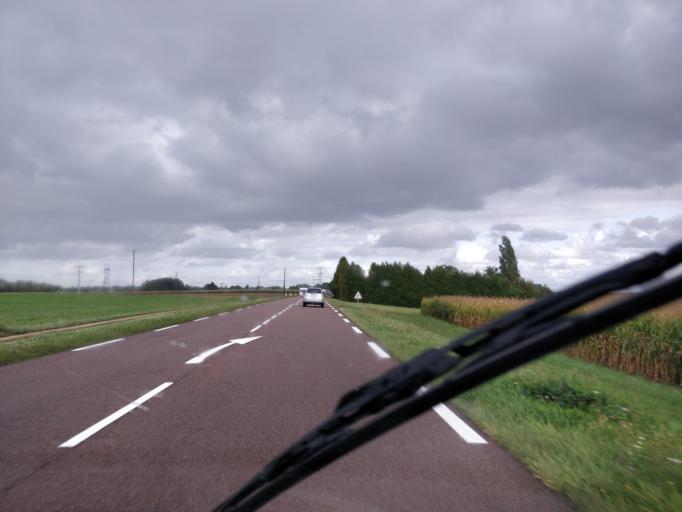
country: FR
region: Champagne-Ardenne
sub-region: Departement de l'Aube
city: Verrieres
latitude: 48.2801
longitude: 4.1916
